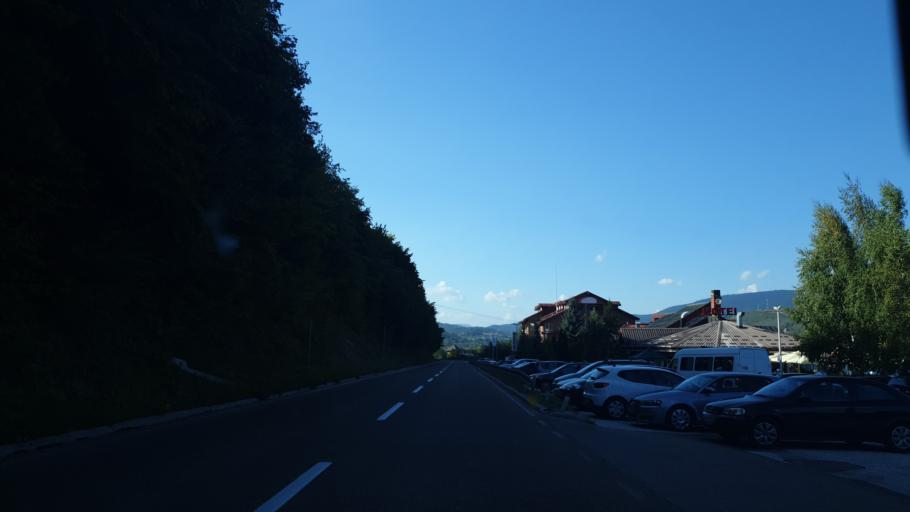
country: RS
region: Central Serbia
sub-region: Zlatiborski Okrug
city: Nova Varos
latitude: 43.5056
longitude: 19.8125
